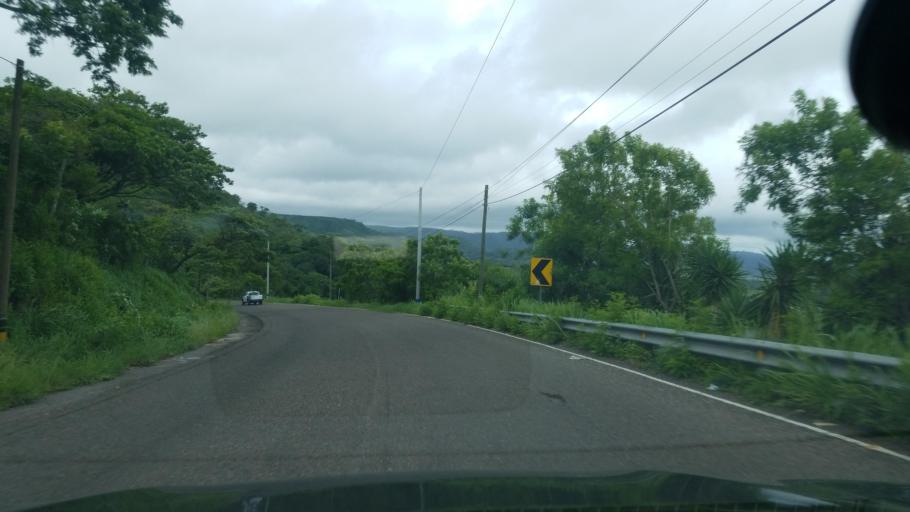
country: HN
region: Choluteca
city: San Marcos de Colon
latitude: 13.4331
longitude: -86.8275
